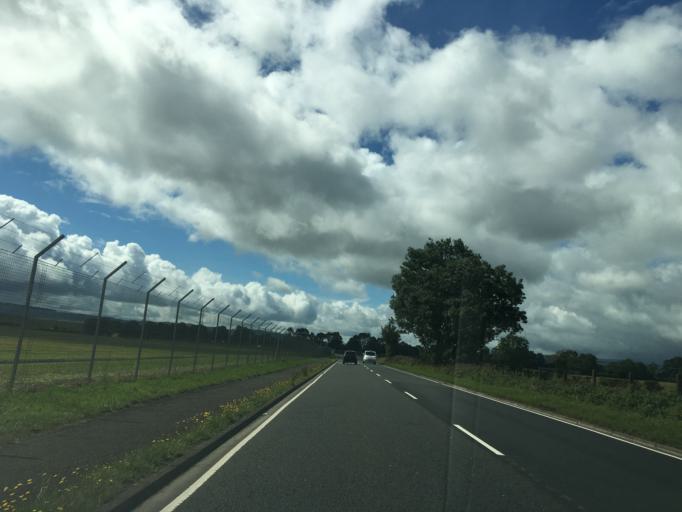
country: GB
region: Scotland
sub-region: Renfrewshire
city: Inchinnan
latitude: 55.8645
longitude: -4.4527
